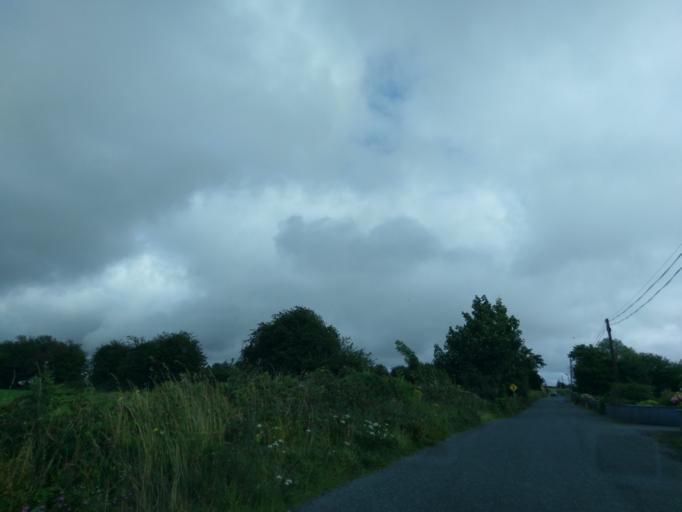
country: IE
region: Connaught
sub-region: County Galway
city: Athenry
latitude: 53.3179
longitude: -8.7764
